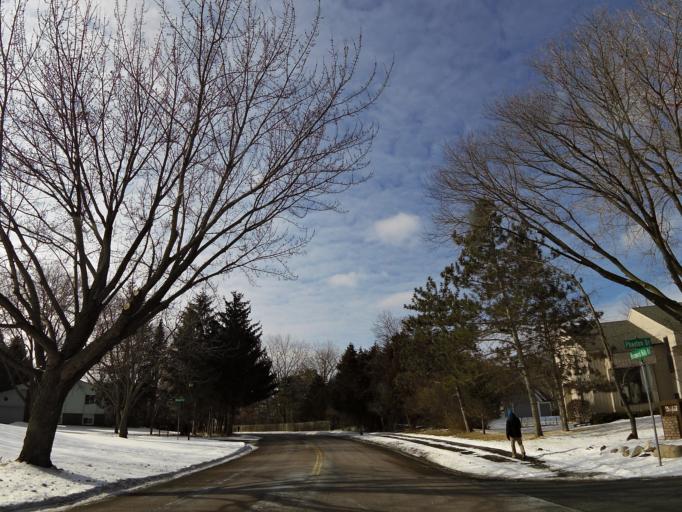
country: US
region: Minnesota
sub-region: Hennepin County
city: Eden Prairie
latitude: 44.8172
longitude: -93.4216
